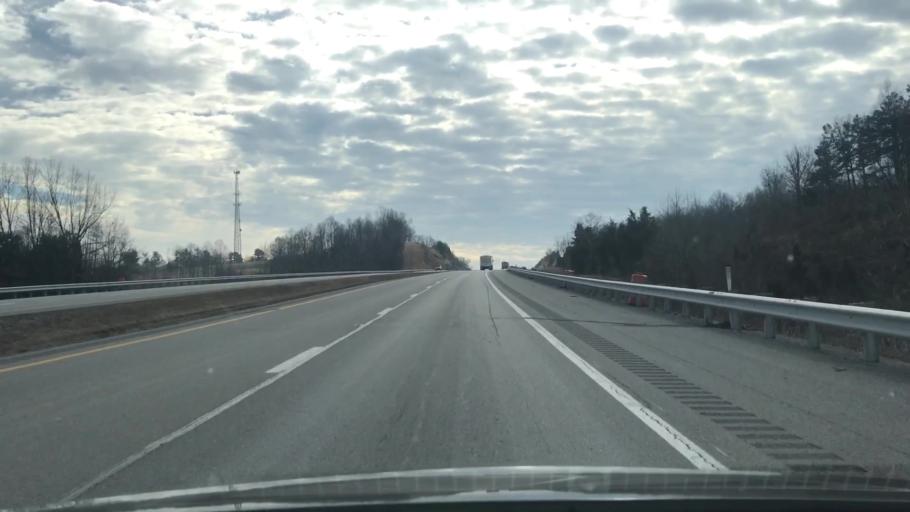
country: US
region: Kentucky
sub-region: Ohio County
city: Hartford
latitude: 37.5309
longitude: -86.9226
